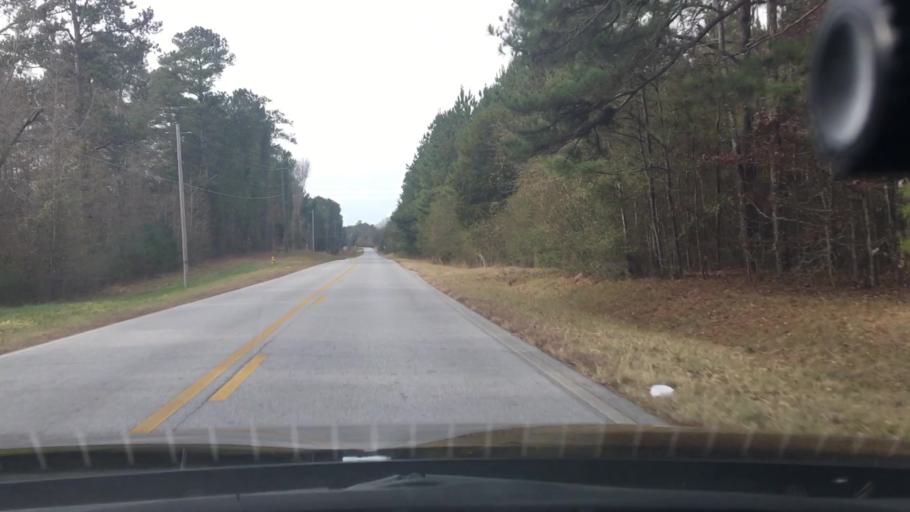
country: US
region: Georgia
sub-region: Spalding County
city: Experiment
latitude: 33.2699
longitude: -84.3436
